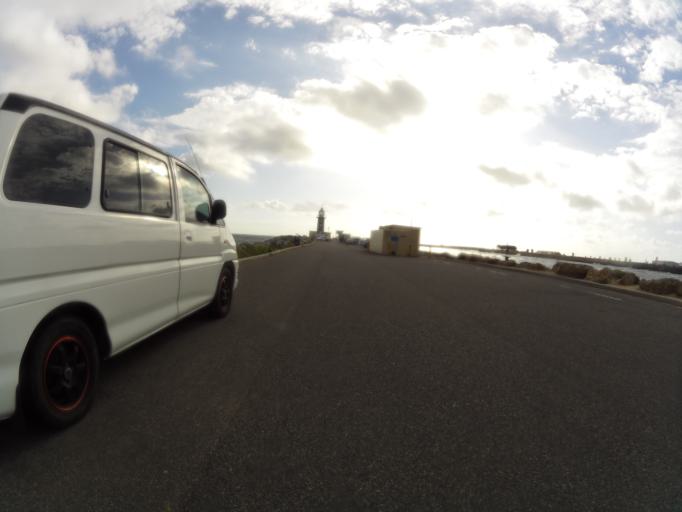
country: AU
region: Western Australia
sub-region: Fremantle
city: South Fremantle
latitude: -32.0558
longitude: 115.7339
